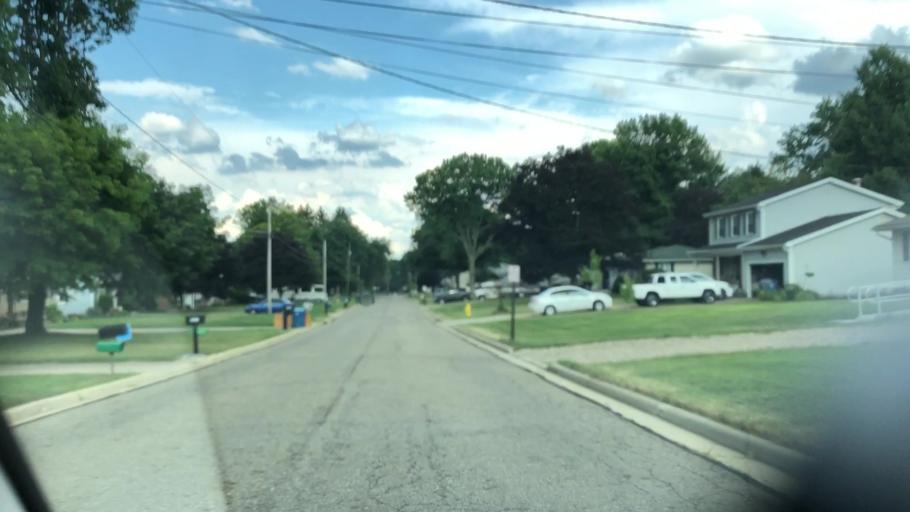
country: US
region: Ohio
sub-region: Summit County
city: Norton
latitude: 41.0367
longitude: -81.6310
